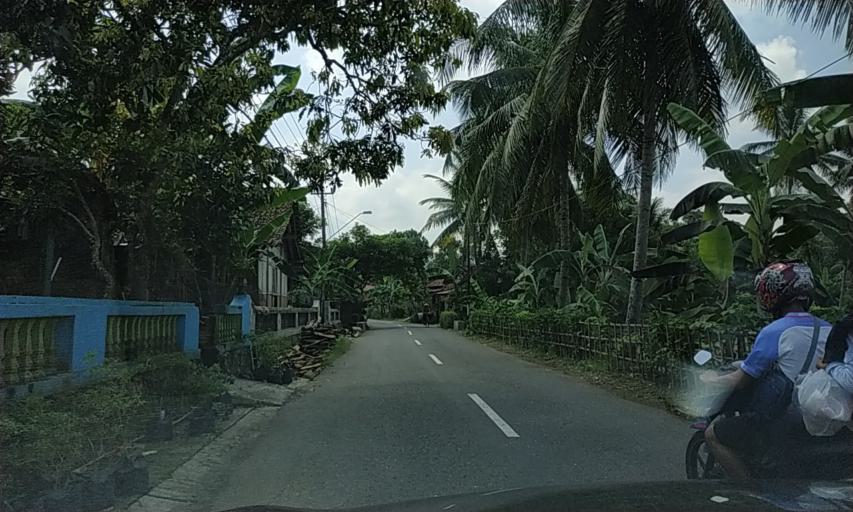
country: ID
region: Central Java
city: Gombong
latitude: -7.6308
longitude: 109.7161
